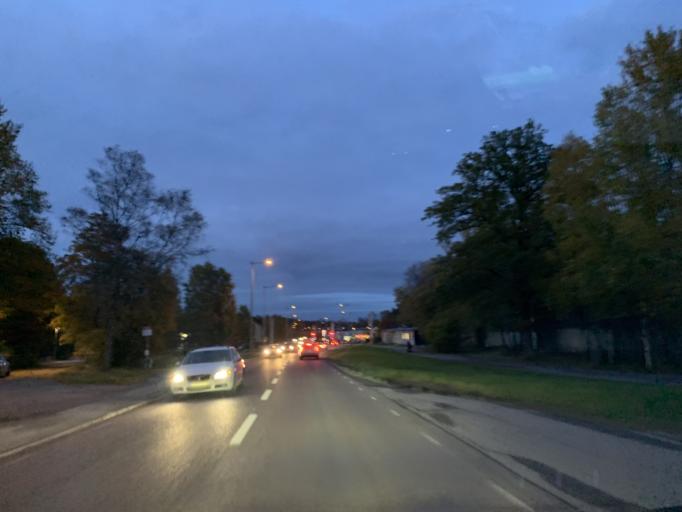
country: SE
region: Stockholm
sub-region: Botkyrka Kommun
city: Tumba
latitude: 59.1884
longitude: 17.8195
